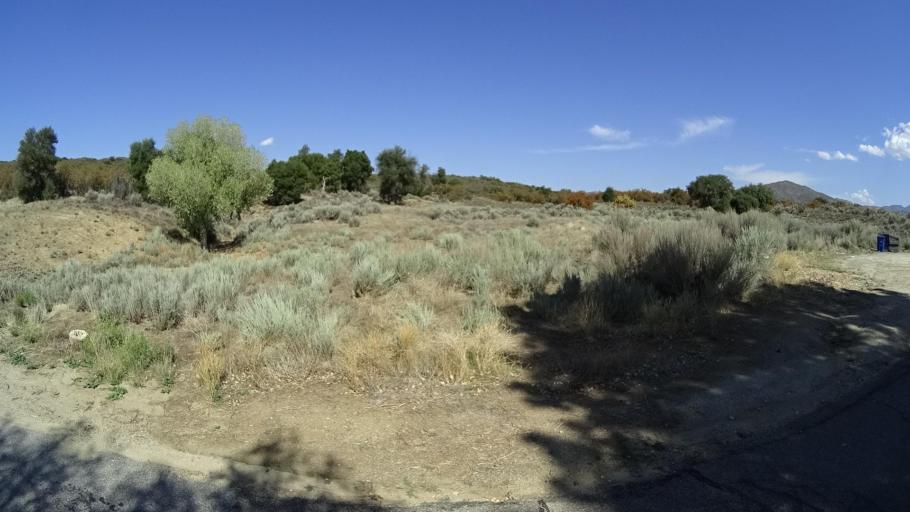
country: US
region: California
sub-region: Riverside County
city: Aguanga
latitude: 33.3108
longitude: -116.6941
